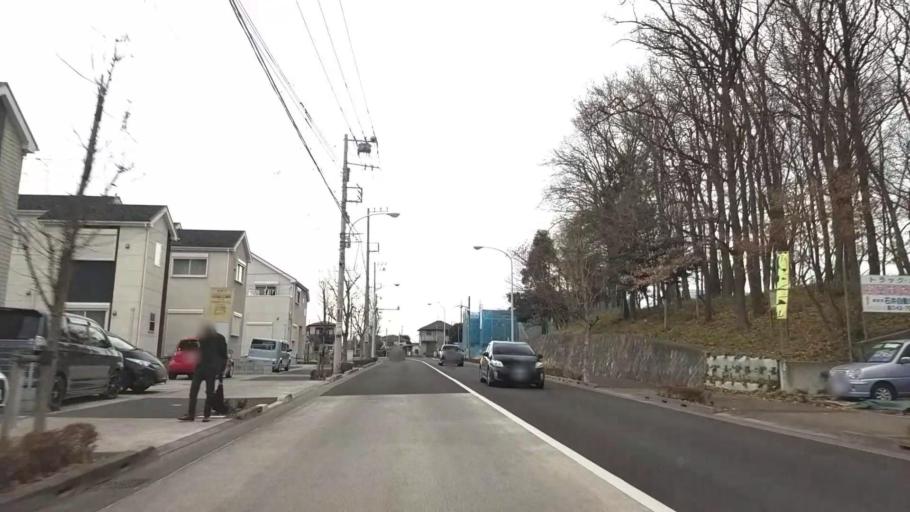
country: JP
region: Tokyo
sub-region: Machida-shi
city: Machida
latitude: 35.5229
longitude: 139.4617
